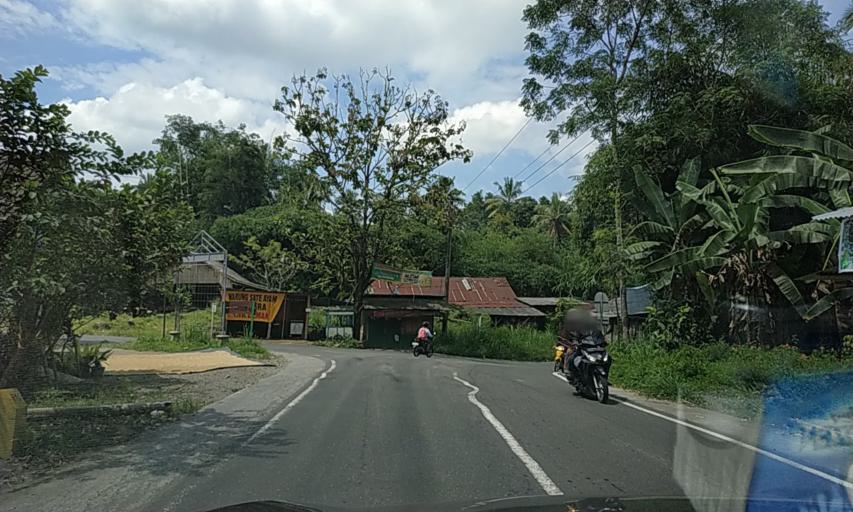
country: ID
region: Central Java
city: Jogonalan
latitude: -7.6487
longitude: 110.4707
